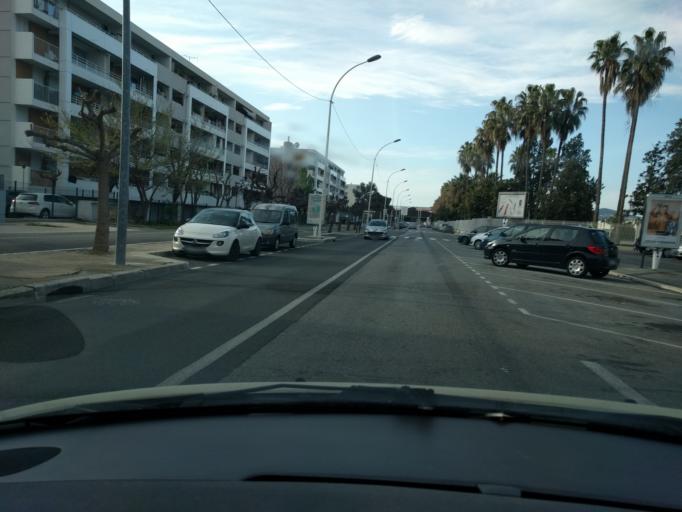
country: FR
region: Provence-Alpes-Cote d'Azur
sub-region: Departement des Alpes-Maritimes
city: Mandelieu-la-Napoule
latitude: 43.5524
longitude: 6.9660
